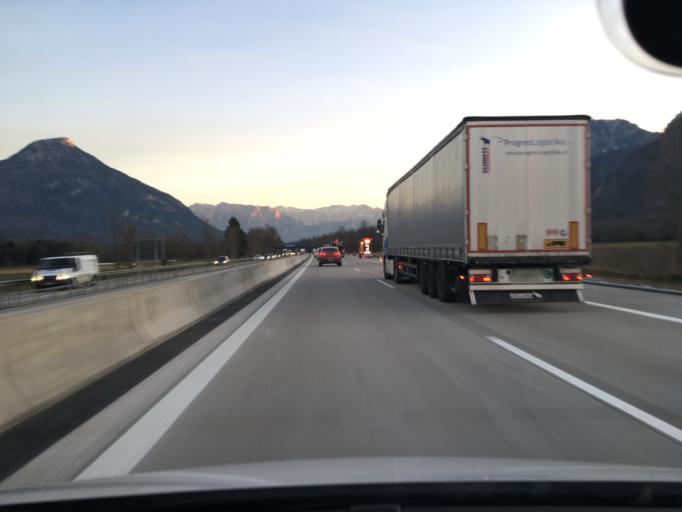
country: DE
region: Bavaria
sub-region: Upper Bavaria
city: Flintsbach
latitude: 47.7279
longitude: 12.1354
